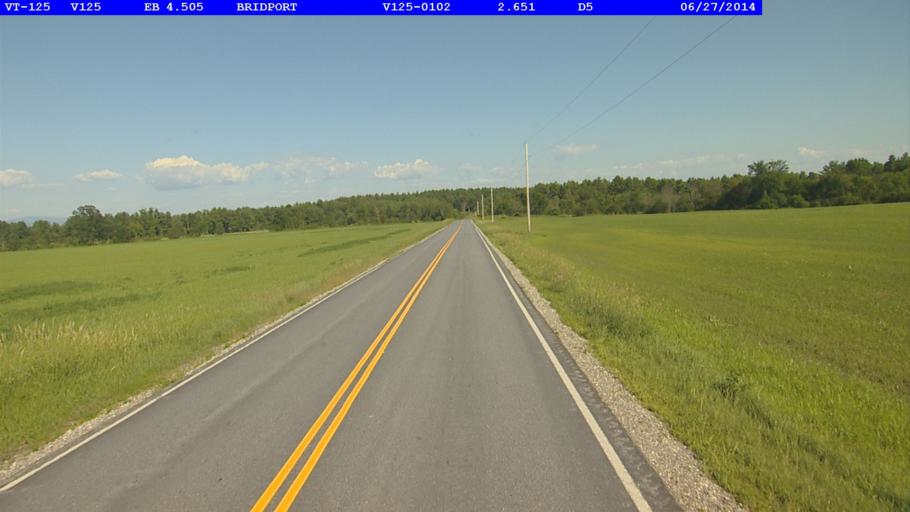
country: US
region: New York
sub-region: Essex County
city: Port Henry
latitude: 43.9996
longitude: -73.3569
